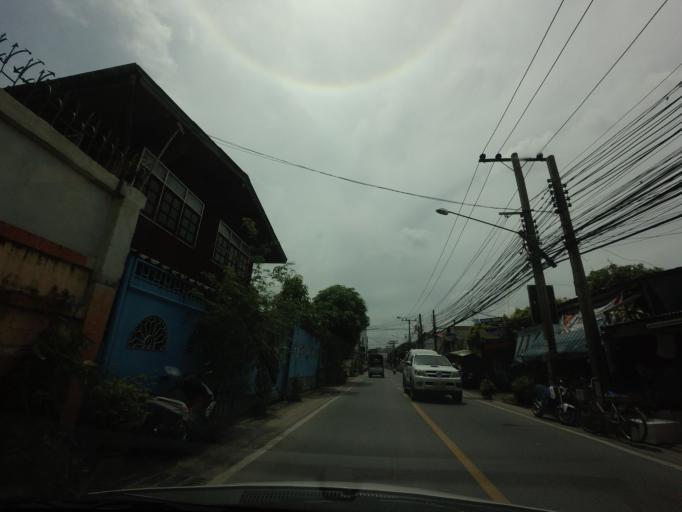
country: TH
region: Samut Prakan
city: Phra Pradaeng
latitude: 13.6494
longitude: 100.5189
